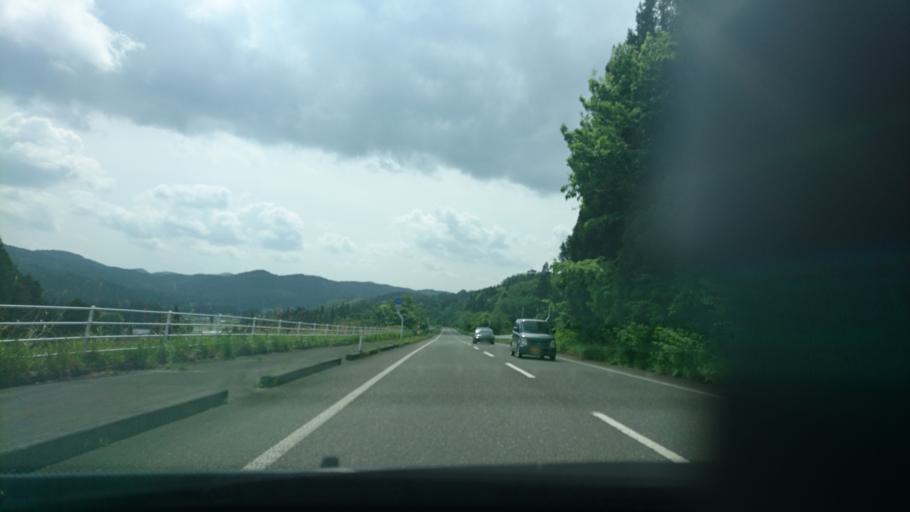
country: JP
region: Iwate
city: Ichinoseki
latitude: 38.8989
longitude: 140.9301
